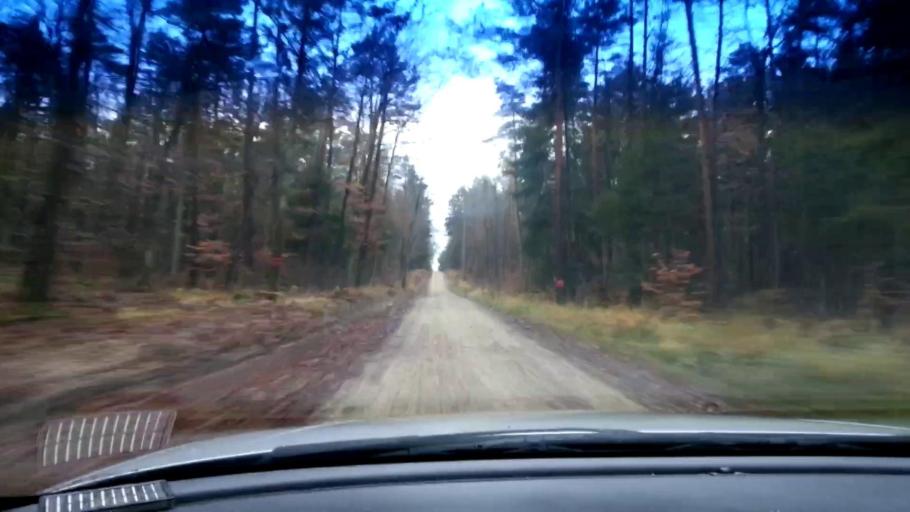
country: DE
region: Bavaria
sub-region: Upper Franconia
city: Breitengussbach
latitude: 49.9549
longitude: 10.9011
